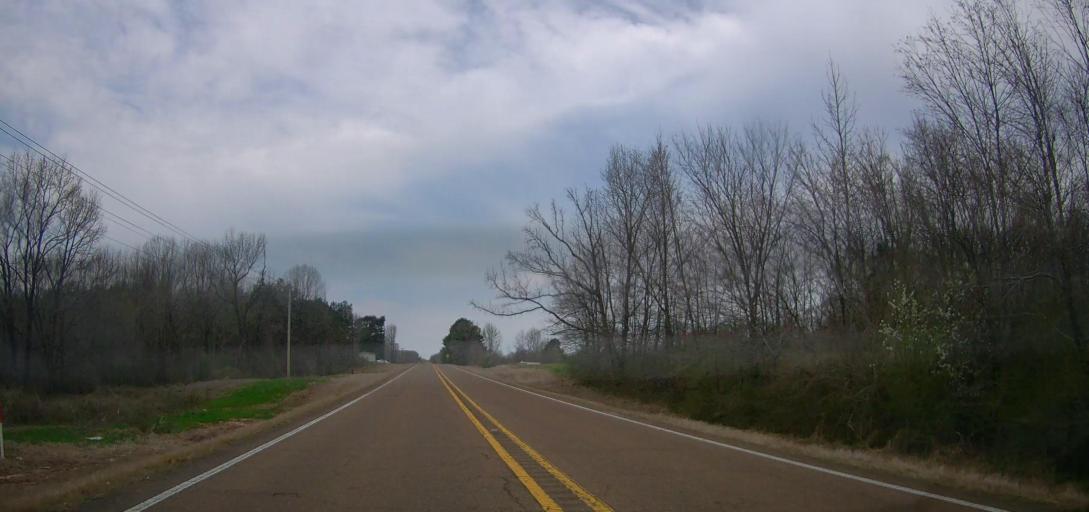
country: US
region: Mississippi
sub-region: Marshall County
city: Byhalia
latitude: 34.8530
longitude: -89.6372
